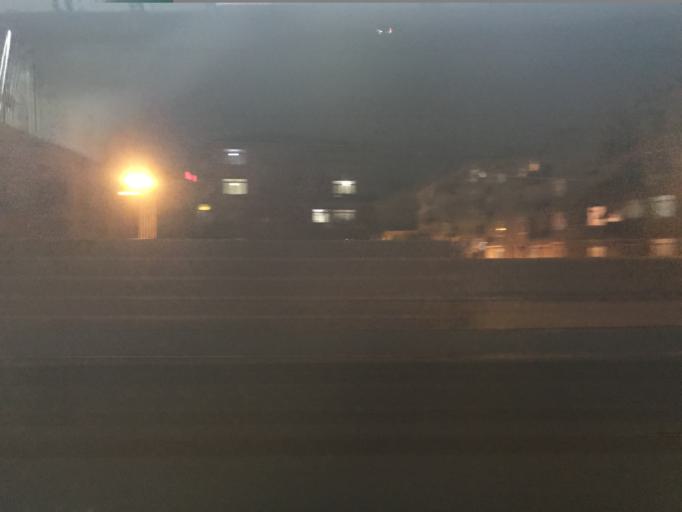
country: TR
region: Istanbul
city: Pendik
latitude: 40.8804
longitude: 29.2370
